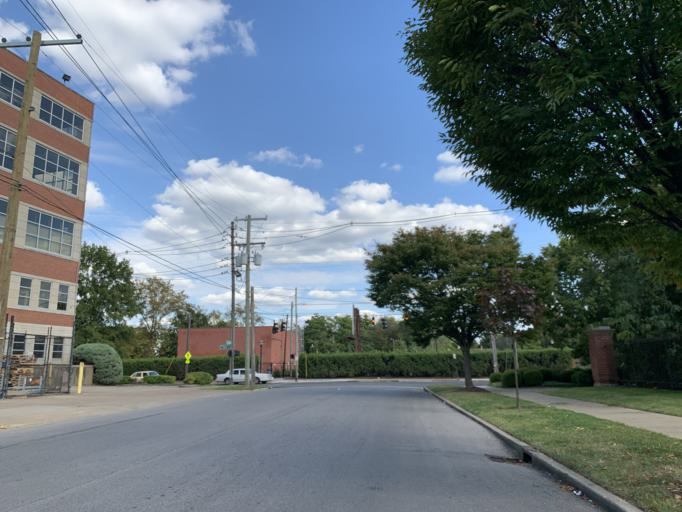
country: US
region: Kentucky
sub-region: Jefferson County
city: Louisville
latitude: 38.2437
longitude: -85.7849
